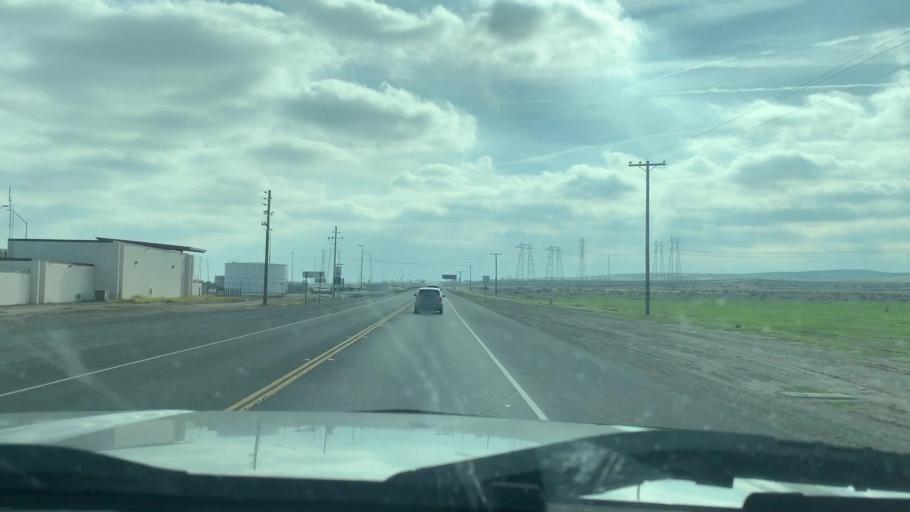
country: US
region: California
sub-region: Kings County
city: Kettleman City
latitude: 36.0059
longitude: -119.9594
